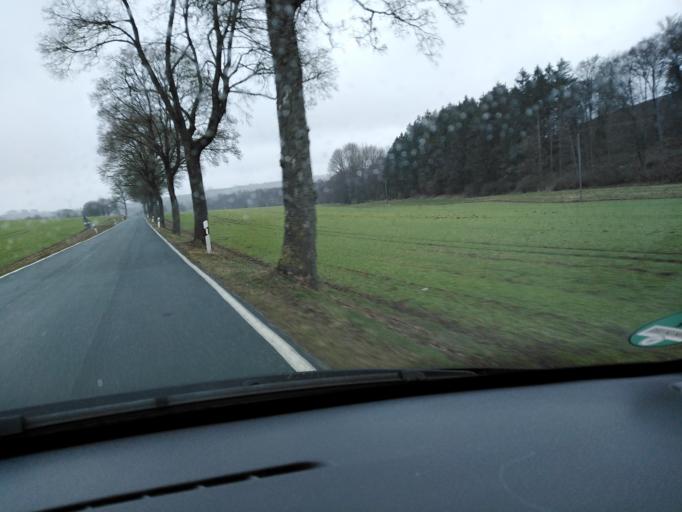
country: DE
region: North Rhine-Westphalia
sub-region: Regierungsbezirk Arnsberg
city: Brilon
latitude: 51.3878
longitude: 8.6347
